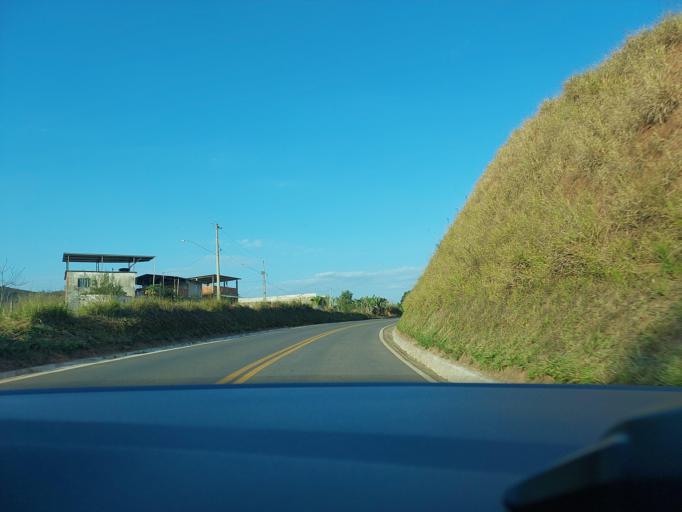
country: BR
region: Minas Gerais
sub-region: Muriae
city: Muriae
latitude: -21.1103
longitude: -42.4505
